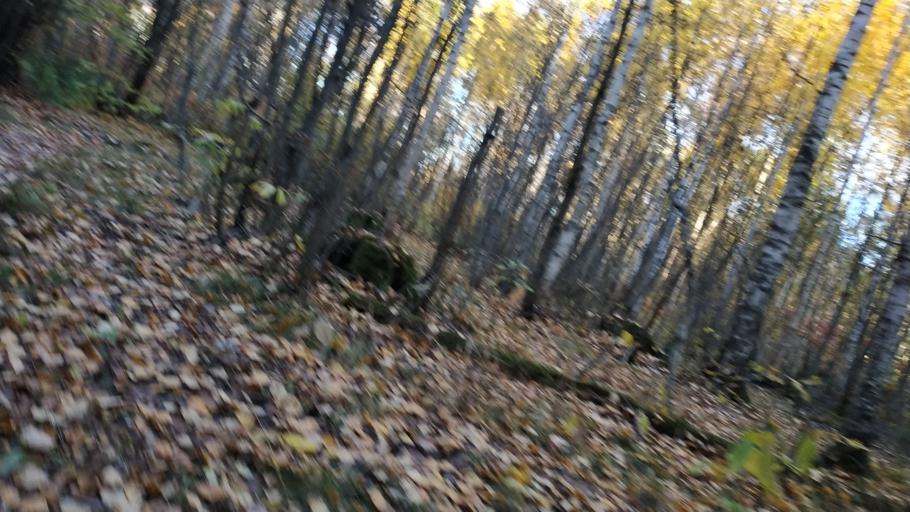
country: RU
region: Moskovskaya
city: Lobnya
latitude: 56.0023
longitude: 37.4627
